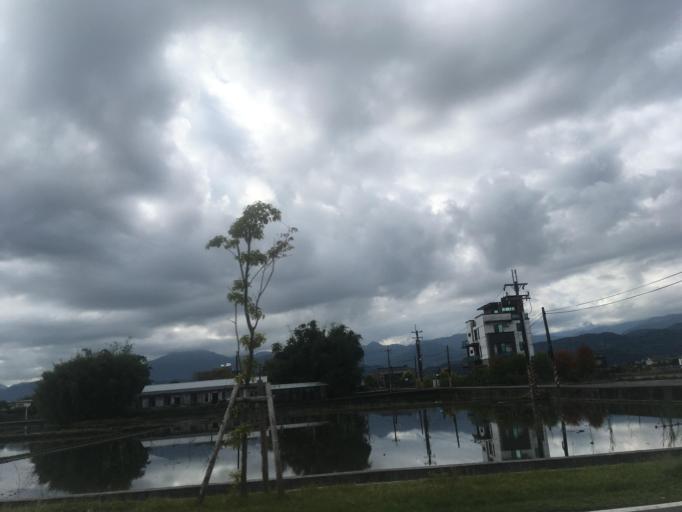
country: TW
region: Taiwan
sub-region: Yilan
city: Yilan
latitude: 24.6859
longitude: 121.7114
